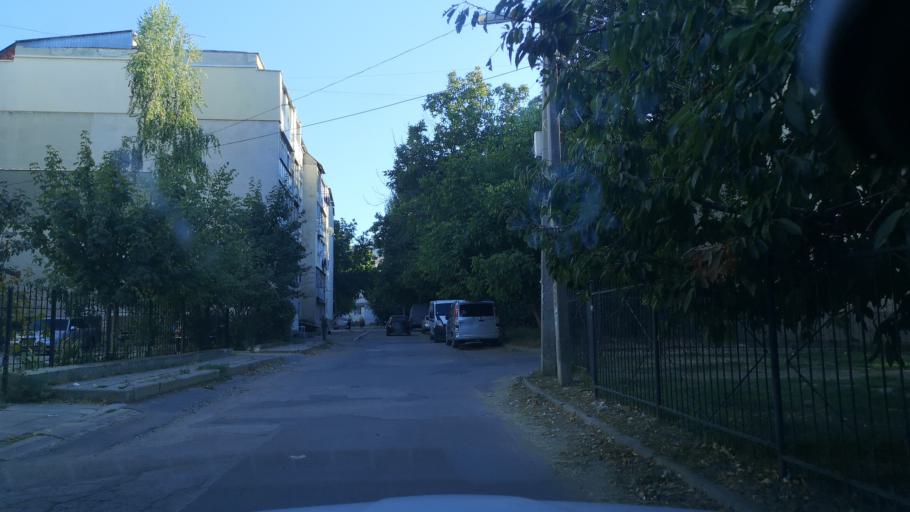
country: MD
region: Chisinau
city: Chisinau
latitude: 46.9885
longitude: 28.8752
